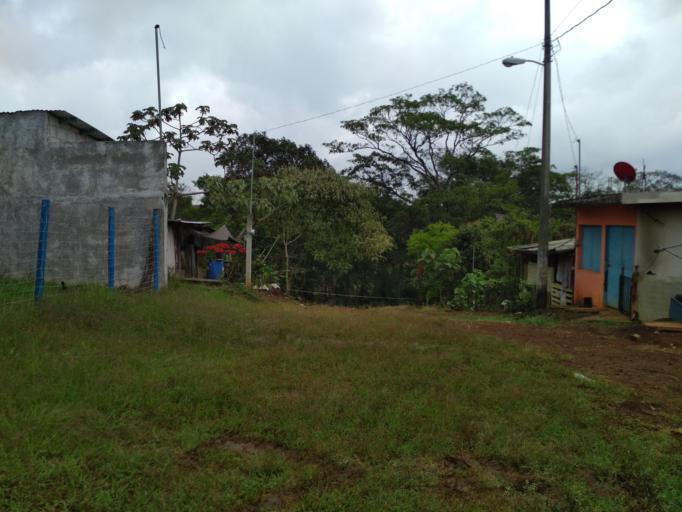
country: MX
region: Veracruz
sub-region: Cordoba
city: San Jose de Tapia
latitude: 18.8501
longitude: -96.9666
